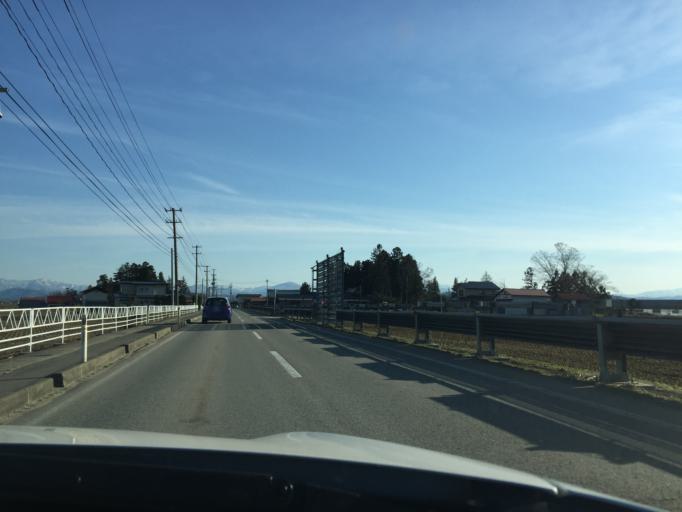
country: JP
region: Yamagata
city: Nagai
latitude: 38.0229
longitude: 140.0564
